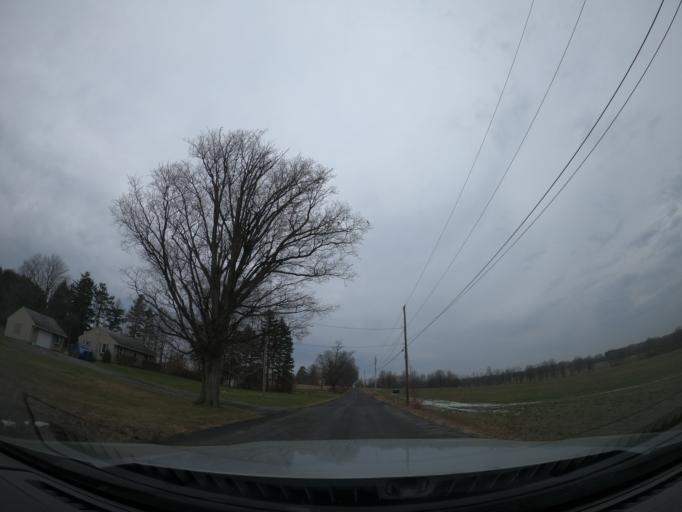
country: US
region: New York
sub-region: Cayuga County
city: Melrose Park
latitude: 42.8401
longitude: -76.5353
